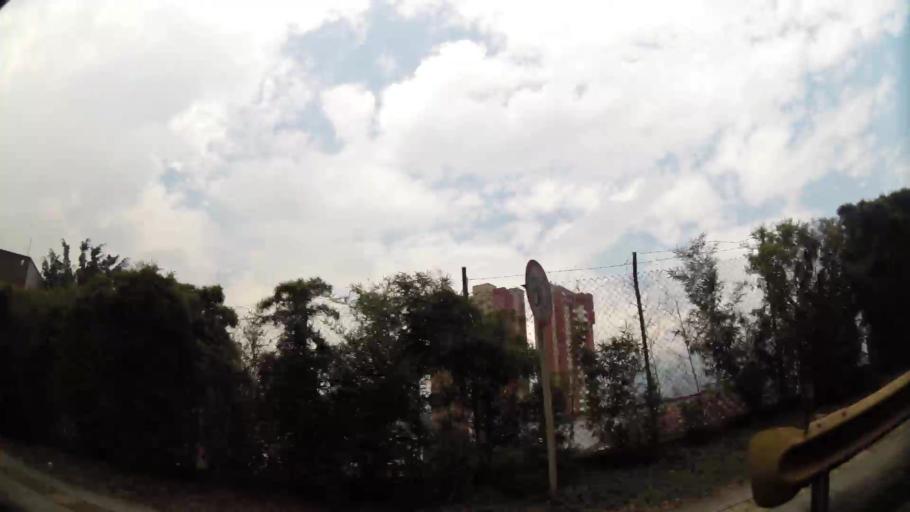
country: CO
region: Antioquia
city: Medellin
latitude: 6.2280
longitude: -75.5650
